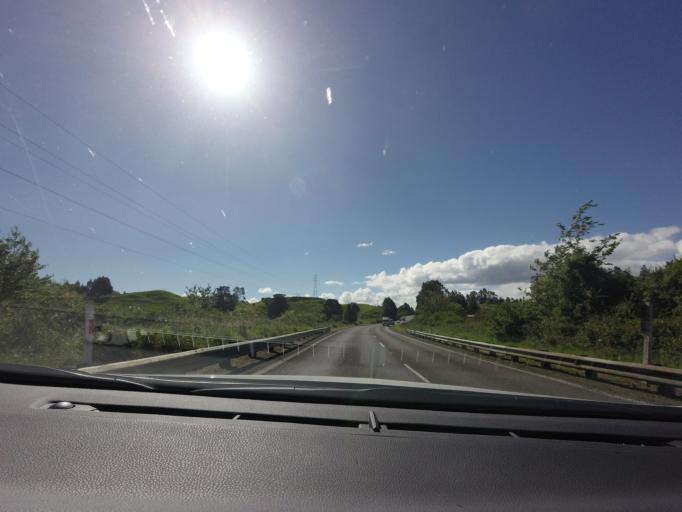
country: NZ
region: Bay of Plenty
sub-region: Rotorua District
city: Rotorua
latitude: -38.0858
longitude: 176.1902
